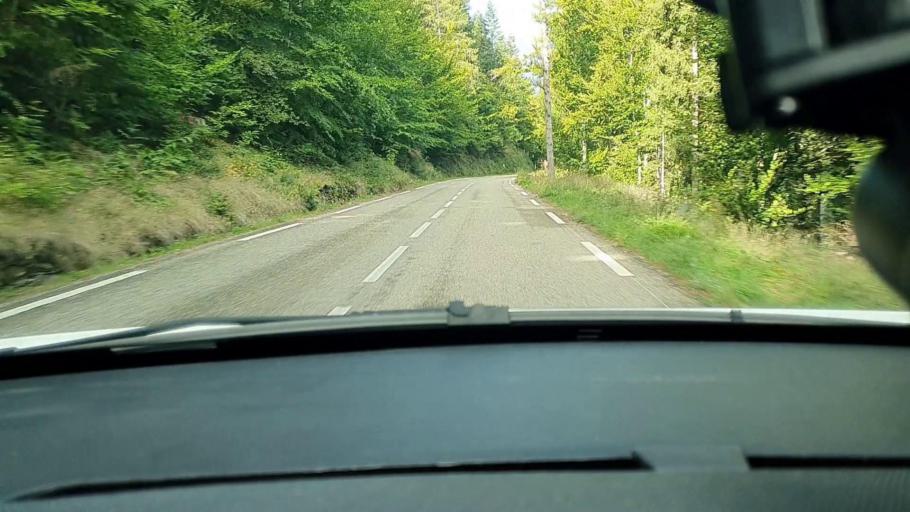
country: FR
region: Rhone-Alpes
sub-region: Departement de l'Ardeche
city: Les Vans
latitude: 44.4285
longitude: 4.0068
